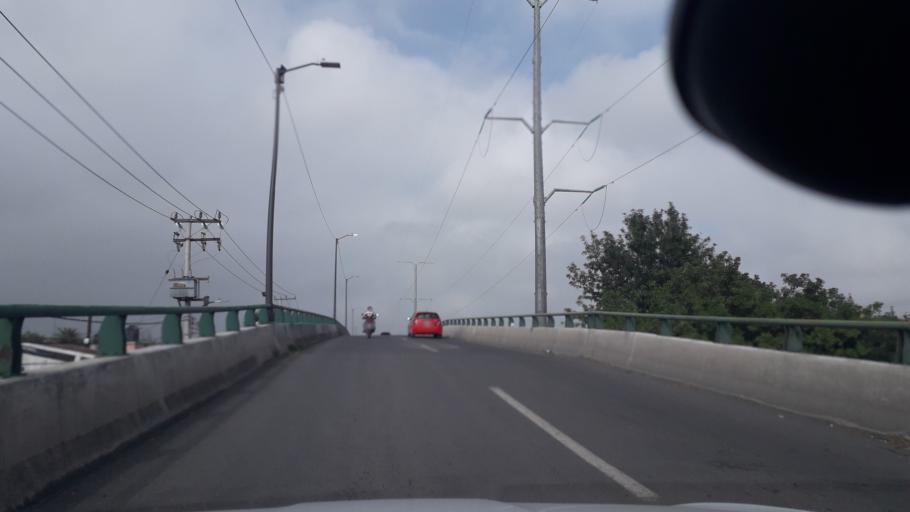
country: MX
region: Mexico
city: Coacalco
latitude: 19.6446
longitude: -99.0966
